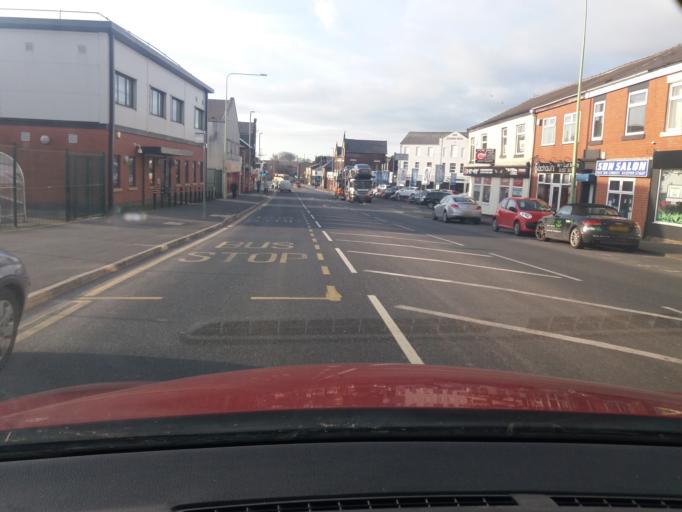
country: GB
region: England
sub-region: Lancashire
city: Chorley
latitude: 53.6483
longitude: -2.6290
